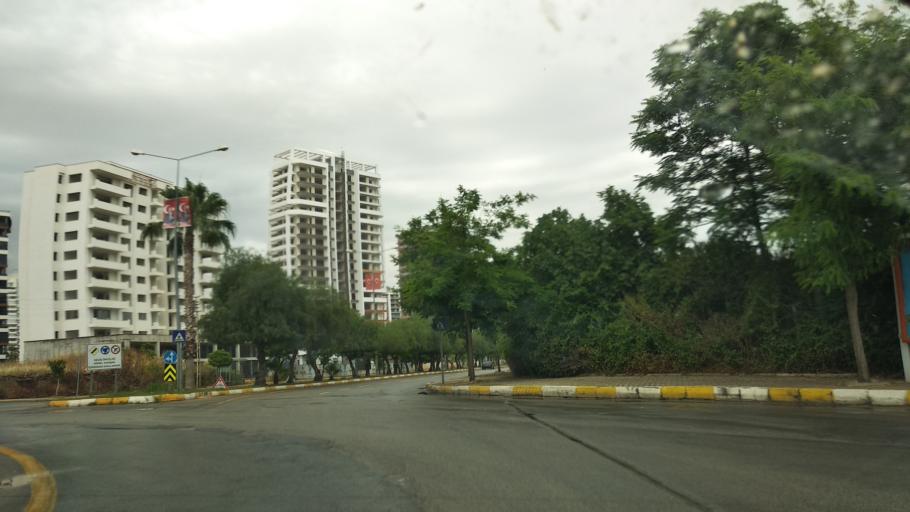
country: TR
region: Mersin
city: Mercin
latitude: 36.7959
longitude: 34.5866
